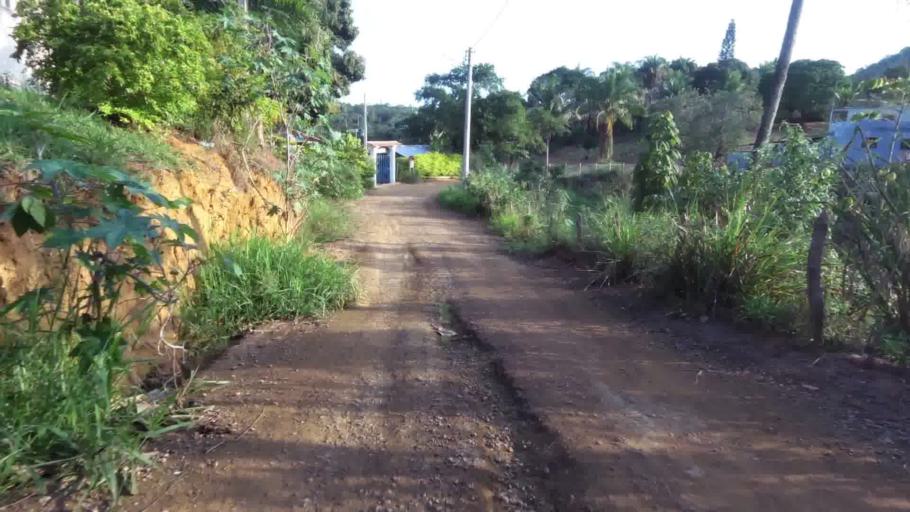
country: BR
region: Espirito Santo
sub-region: Guarapari
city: Guarapari
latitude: -20.7422
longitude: -40.6111
